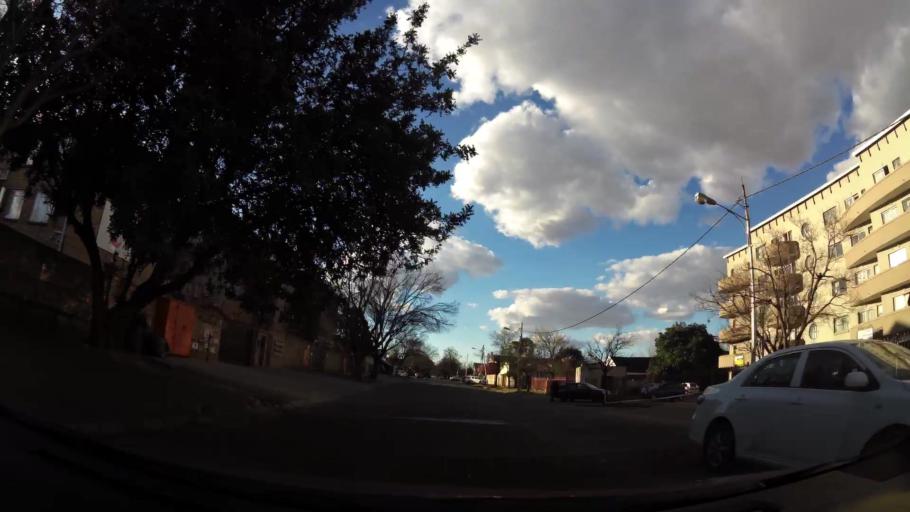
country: ZA
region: North-West
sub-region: Dr Kenneth Kaunda District Municipality
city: Potchefstroom
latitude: -26.7011
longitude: 27.0887
